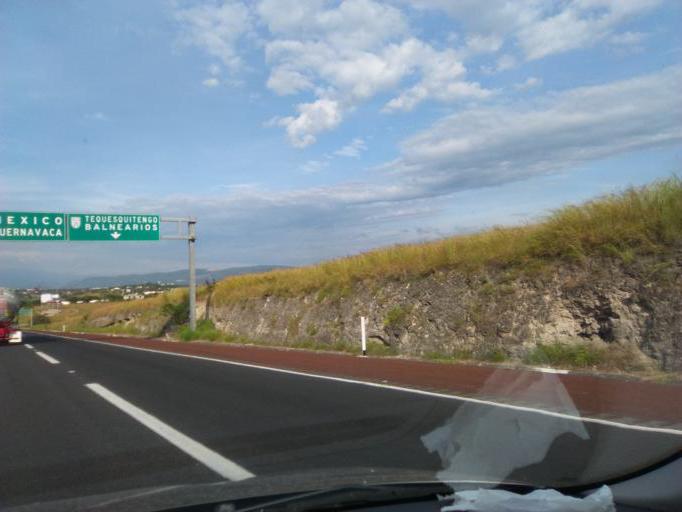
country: MX
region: Morelos
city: Alpuyeca
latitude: 18.7164
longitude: -99.2664
